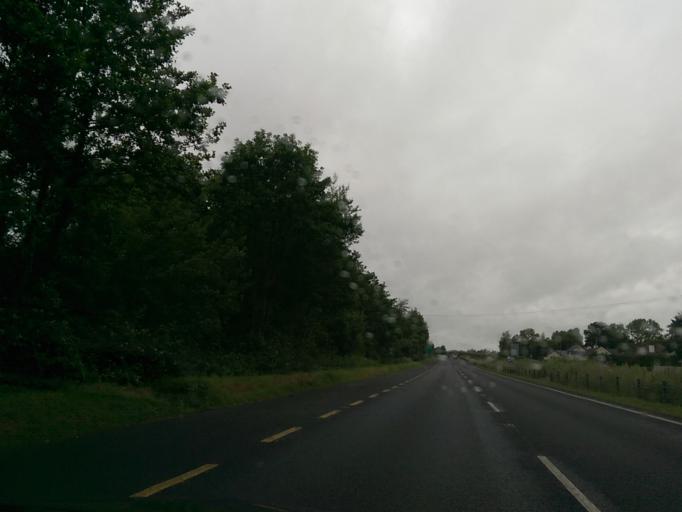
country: IE
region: Munster
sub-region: An Clar
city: Sixmilebridge
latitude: 52.6915
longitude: -8.7514
